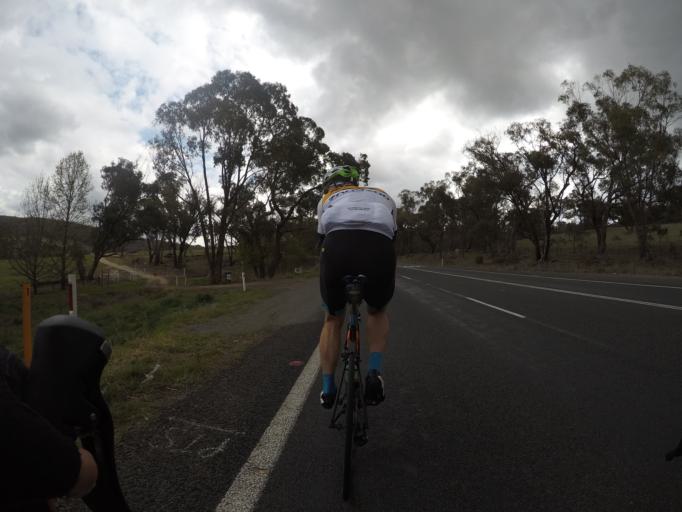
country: AU
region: New South Wales
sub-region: Bathurst Regional
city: Eglinton
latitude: -33.4211
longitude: 149.4127
